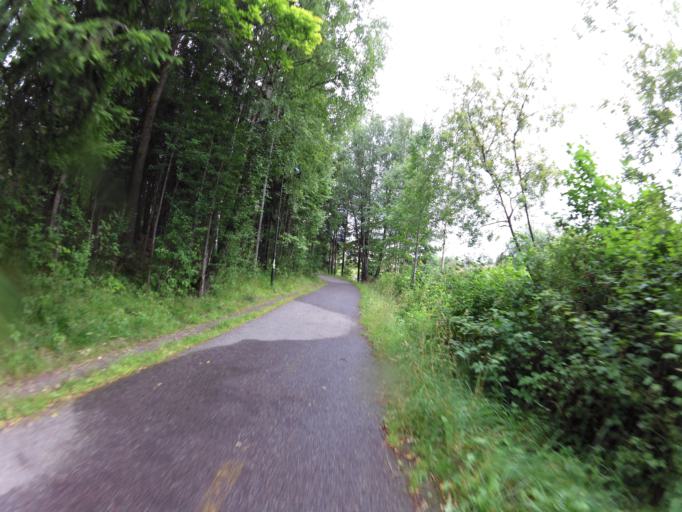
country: NO
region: Ostfold
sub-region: Moss
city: Moss
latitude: 59.4393
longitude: 10.6766
